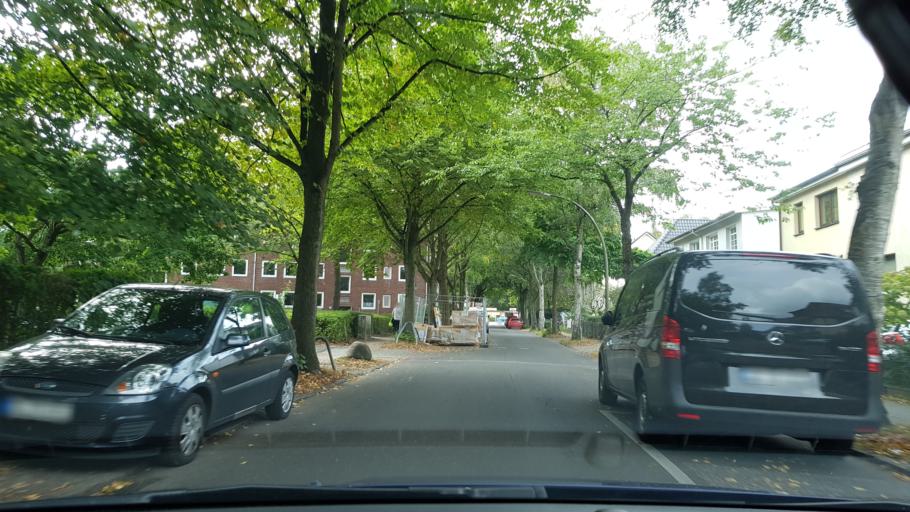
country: DE
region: Hamburg
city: Steilshoop
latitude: 53.6021
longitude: 10.0536
